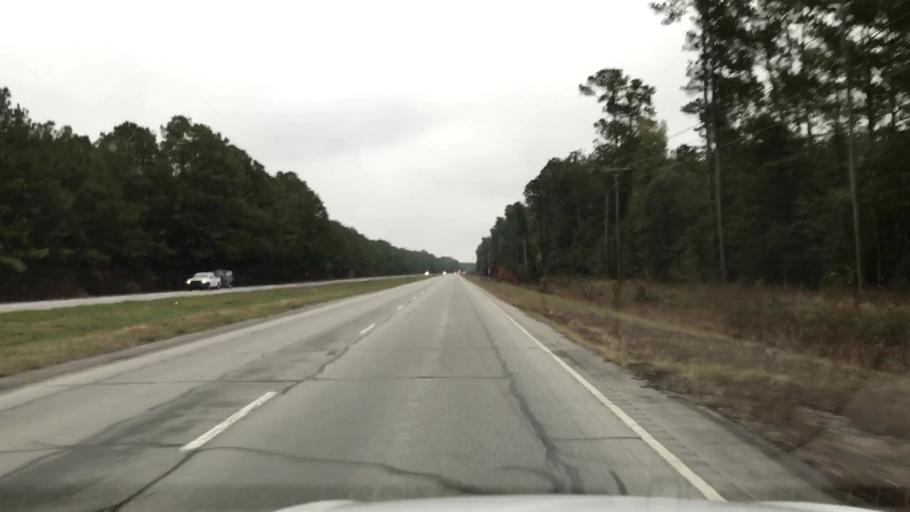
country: US
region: South Carolina
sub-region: Charleston County
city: Awendaw
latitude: 33.0667
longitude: -79.5277
